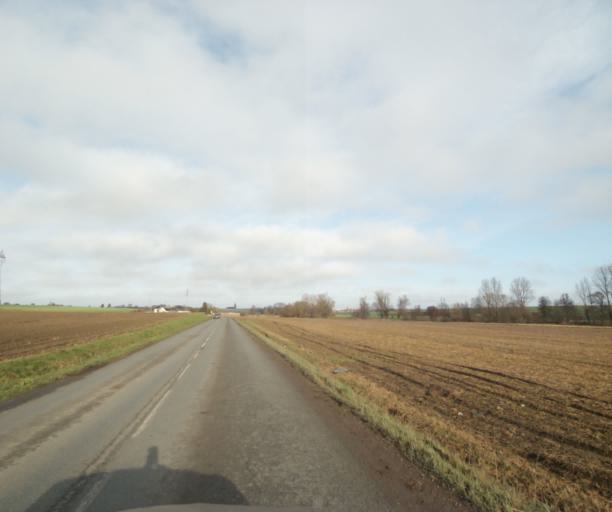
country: FR
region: Nord-Pas-de-Calais
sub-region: Departement du Nord
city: Thiant
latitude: 50.2908
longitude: 3.4484
